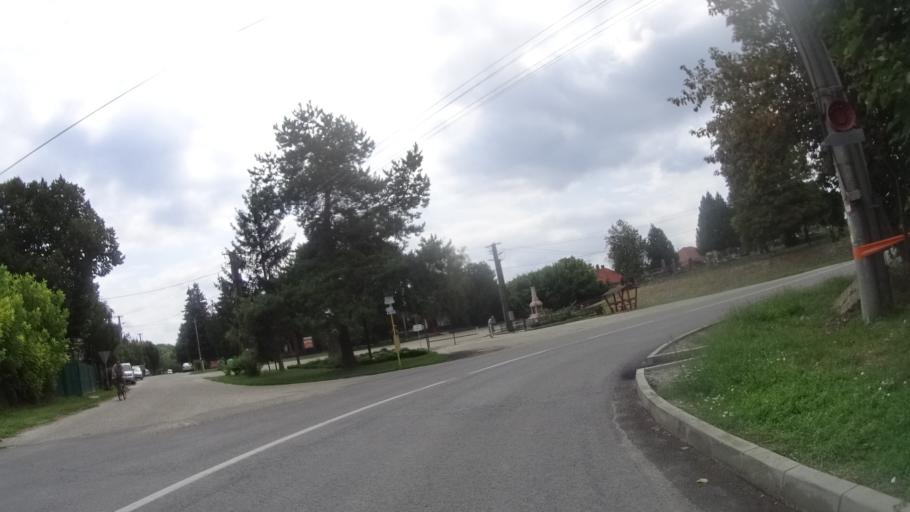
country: HU
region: Gyor-Moson-Sopron
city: Bony
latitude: 47.7519
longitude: 17.8201
